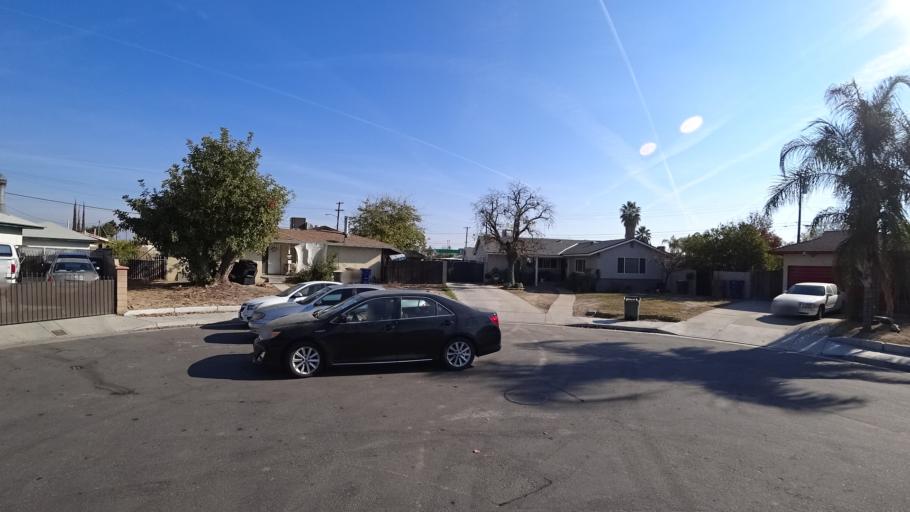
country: US
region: California
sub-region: Kern County
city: Bakersfield
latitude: 35.3313
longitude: -119.0148
